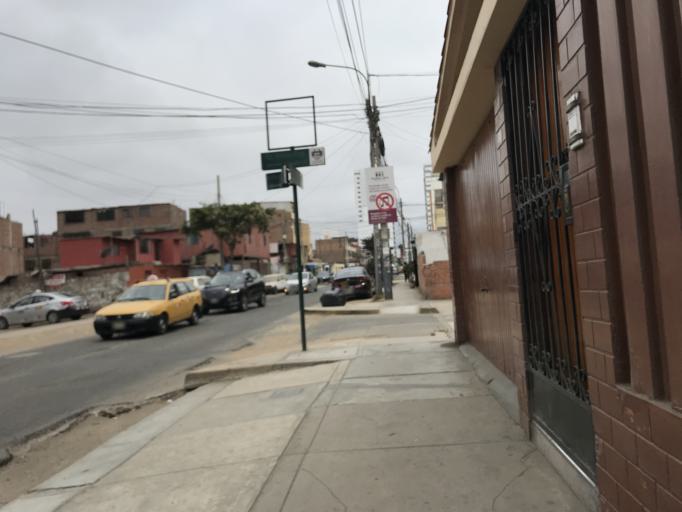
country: PE
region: Lima
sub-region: Lima
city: San Isidro
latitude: -12.0790
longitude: -77.0753
